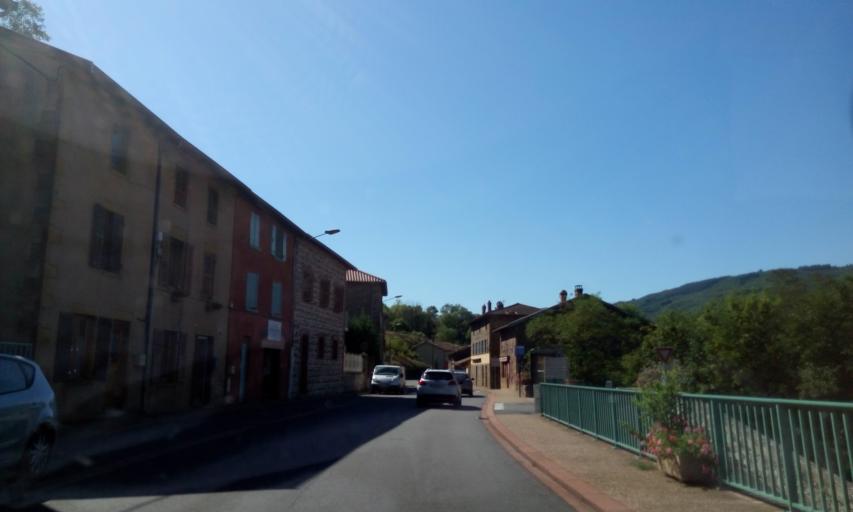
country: FR
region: Rhone-Alpes
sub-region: Departement du Rhone
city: Grandris
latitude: 45.9830
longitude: 4.5090
